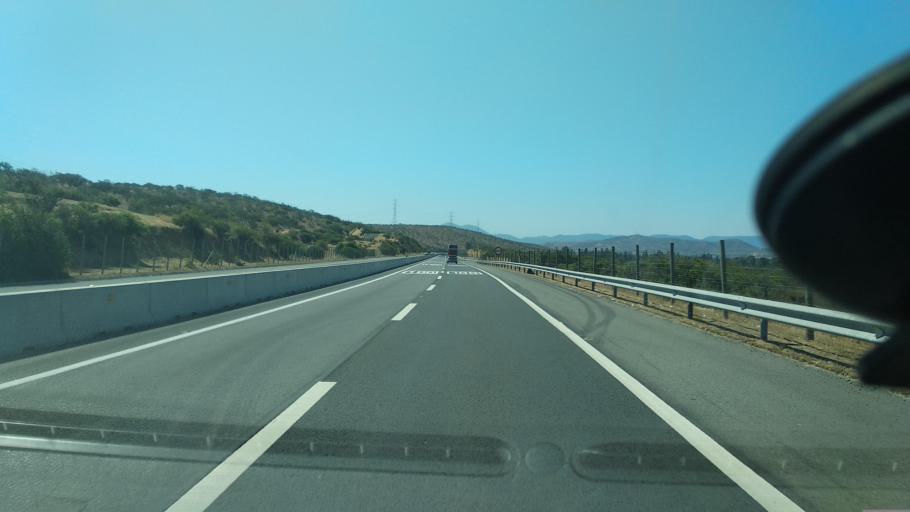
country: CL
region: Valparaiso
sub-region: Provincia de Marga Marga
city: Limache
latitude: -33.0147
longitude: -71.3207
